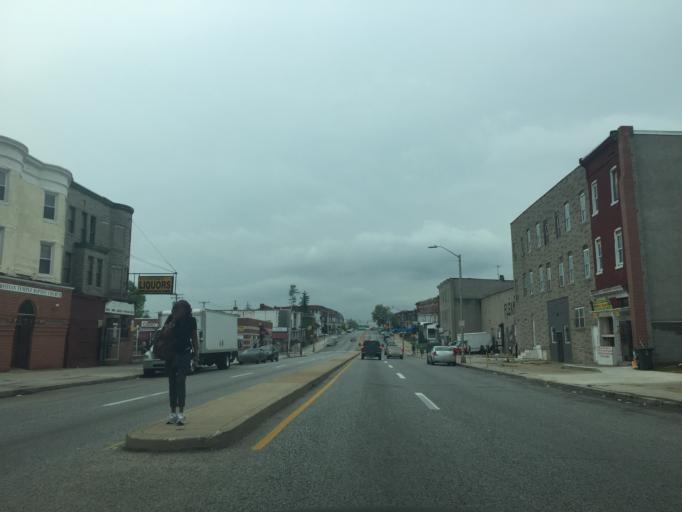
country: US
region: Maryland
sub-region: City of Baltimore
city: Baltimore
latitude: 39.3097
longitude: -76.6513
